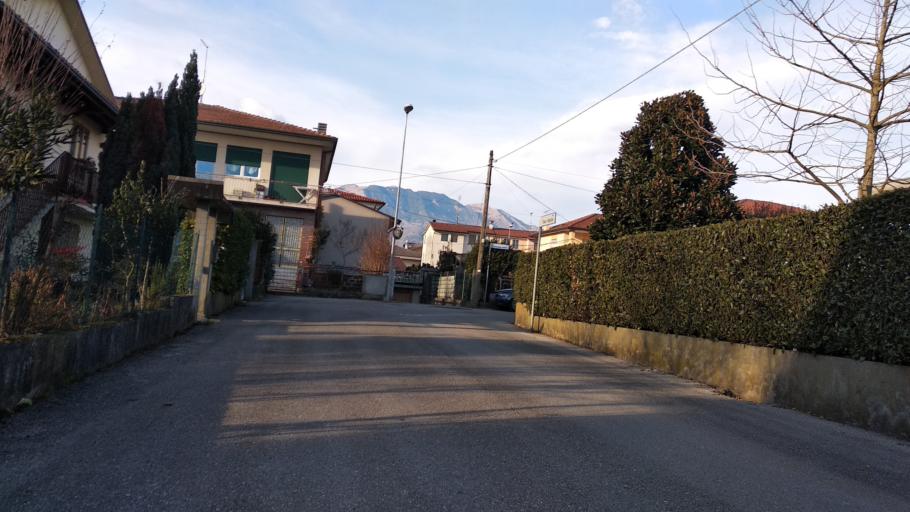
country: IT
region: Veneto
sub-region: Provincia di Vicenza
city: San Vito di Leguzzano
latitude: 45.6915
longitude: 11.3689
